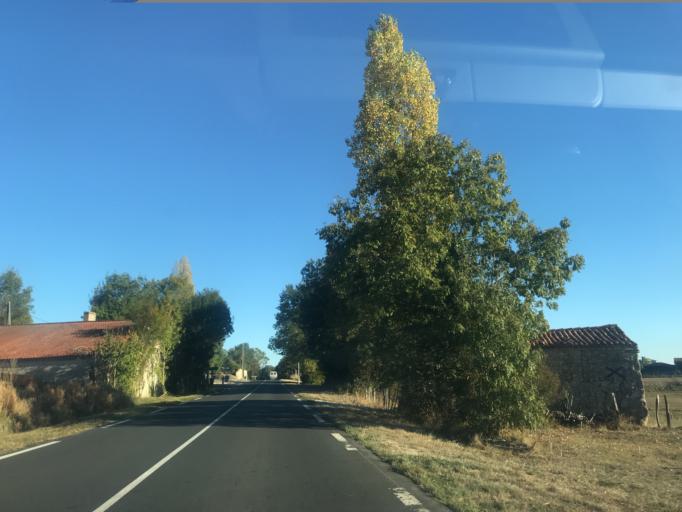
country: FR
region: Poitou-Charentes
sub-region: Departement de la Charente-Maritime
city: Montguyon
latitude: 45.1831
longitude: -0.1278
